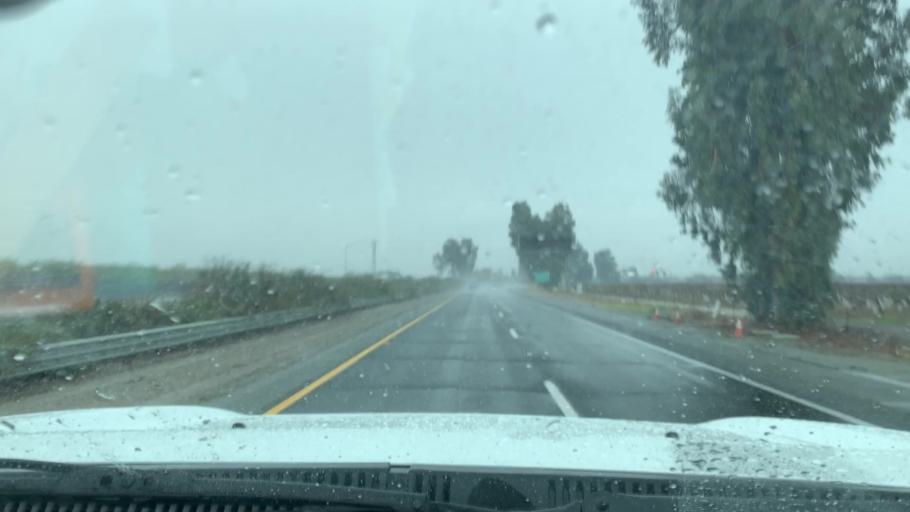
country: US
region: California
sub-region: Tulare County
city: Earlimart
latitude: 35.8673
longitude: -119.2701
